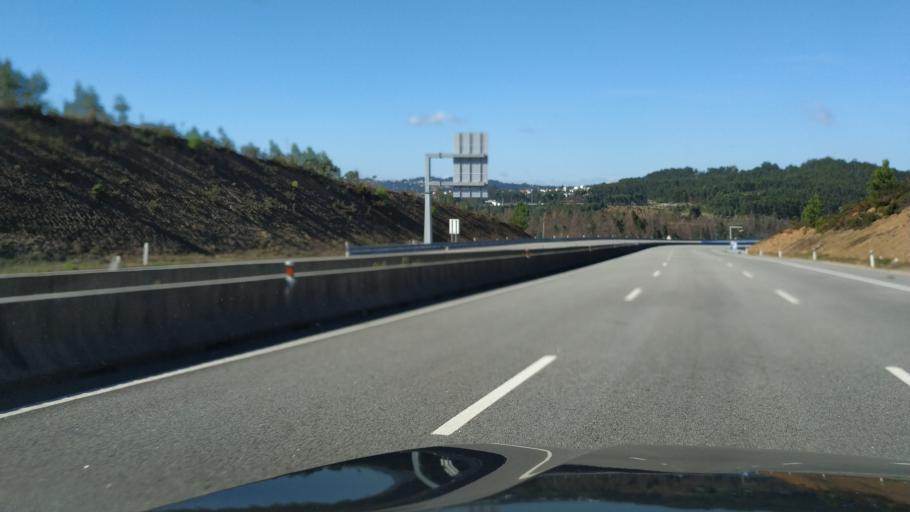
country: PT
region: Porto
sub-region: Vila Nova de Gaia
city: Sandim
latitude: 41.0294
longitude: -8.4842
